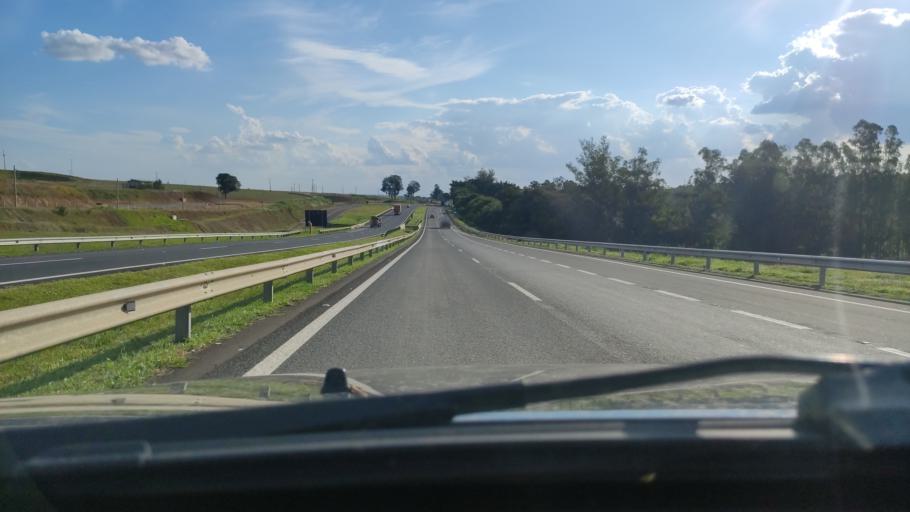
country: BR
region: Sao Paulo
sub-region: Itapira
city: Itapira
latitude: -22.4516
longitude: -46.8527
